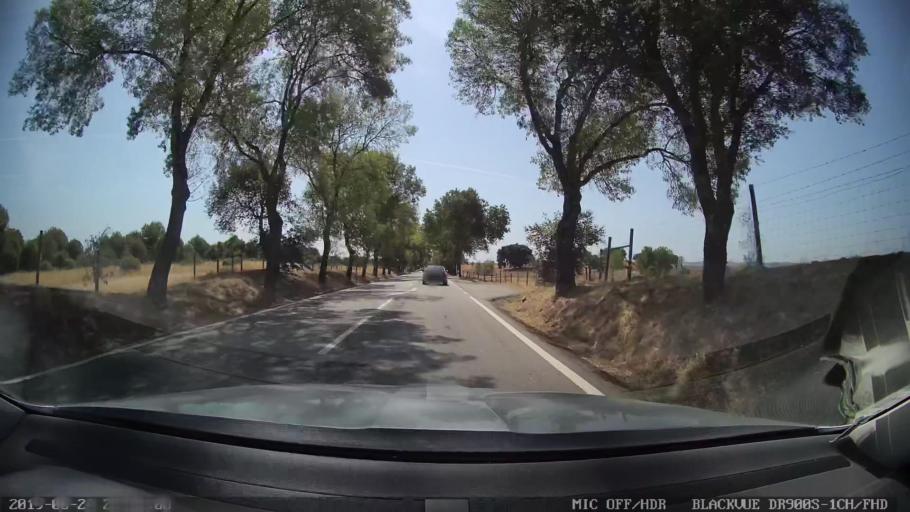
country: PT
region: Castelo Branco
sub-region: Idanha-A-Nova
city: Idanha-a-Nova
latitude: 39.8605
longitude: -7.3160
